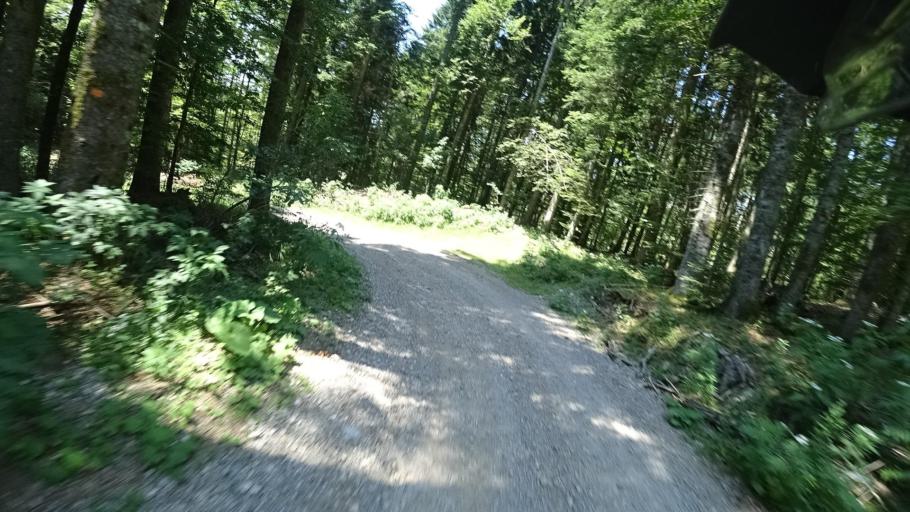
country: HR
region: Primorsko-Goranska
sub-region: Grad Delnice
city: Delnice
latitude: 45.2748
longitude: 14.9163
